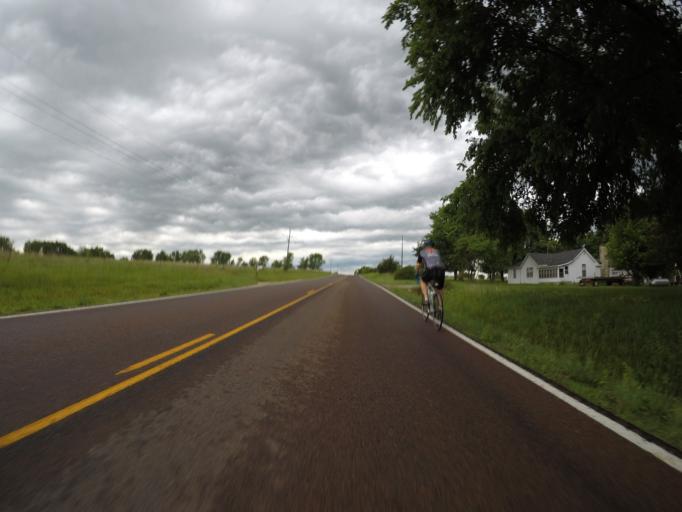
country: US
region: Kansas
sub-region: Shawnee County
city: Auburn
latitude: 38.9644
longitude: -95.9516
